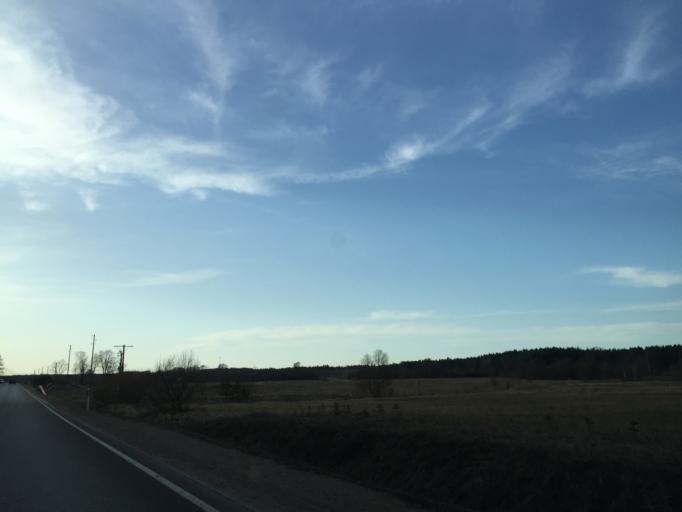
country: LV
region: Ikskile
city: Ikskile
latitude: 56.8947
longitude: 24.4424
